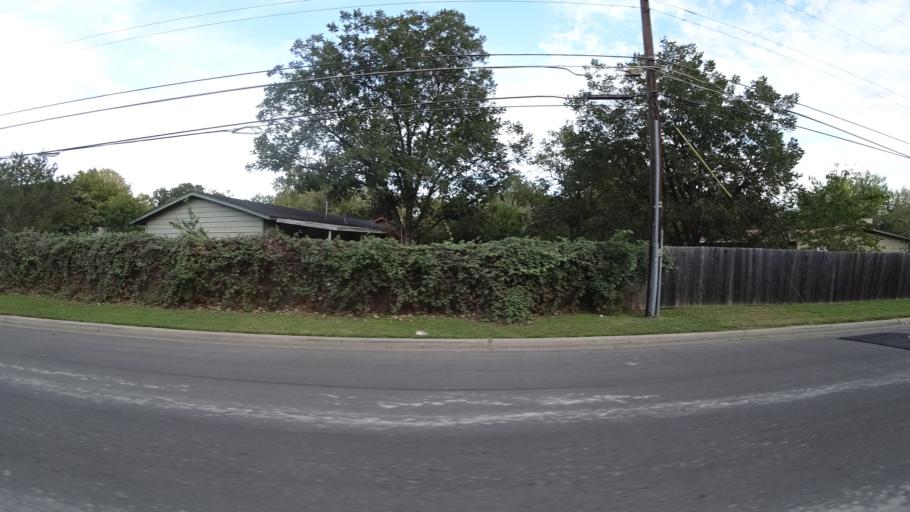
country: US
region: Texas
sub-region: Travis County
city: Austin
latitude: 30.2094
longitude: -97.7680
